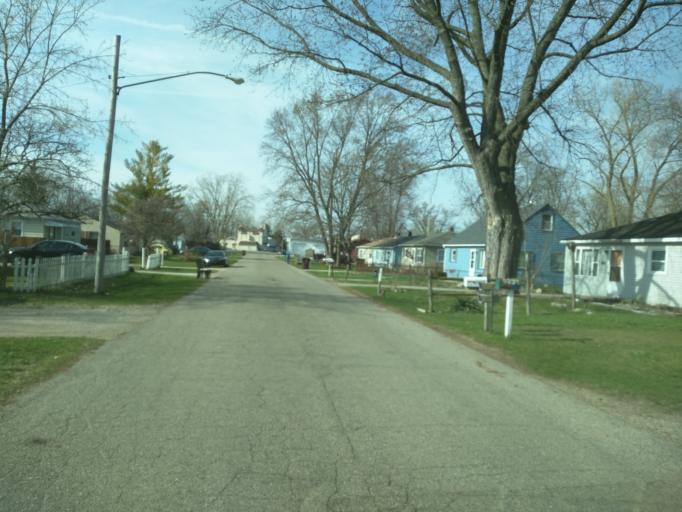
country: US
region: Michigan
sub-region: Ingham County
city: Edgemont Park
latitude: 42.7666
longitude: -84.5963
